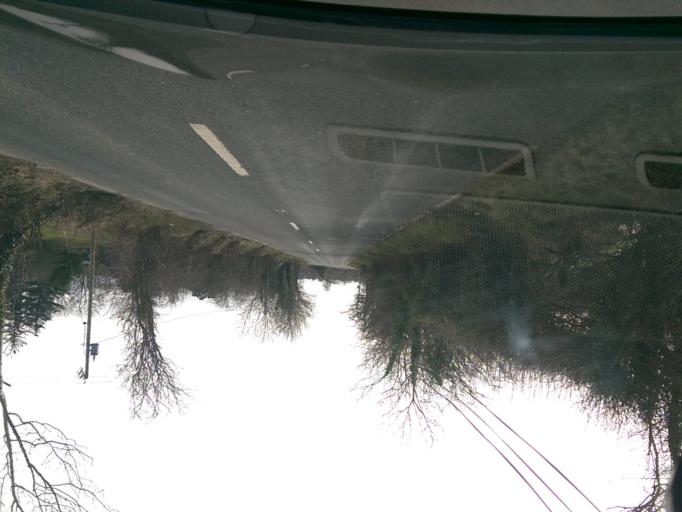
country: IE
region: Connaught
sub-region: County Galway
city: Tuam
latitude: 53.4213
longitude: -8.7892
